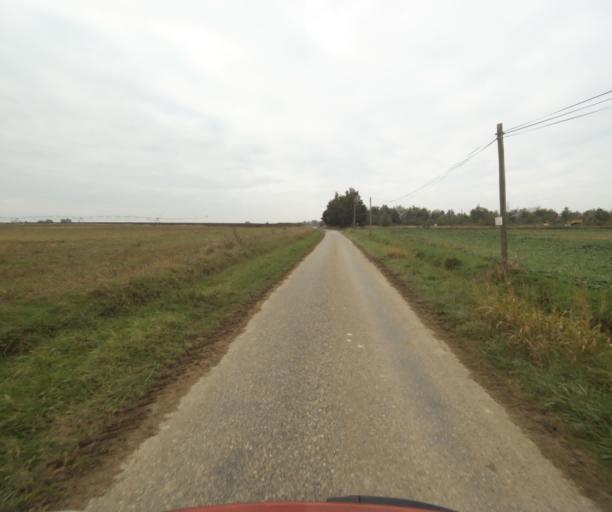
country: FR
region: Midi-Pyrenees
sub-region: Departement du Tarn-et-Garonne
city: Verdun-sur-Garonne
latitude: 43.8129
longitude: 1.1936
